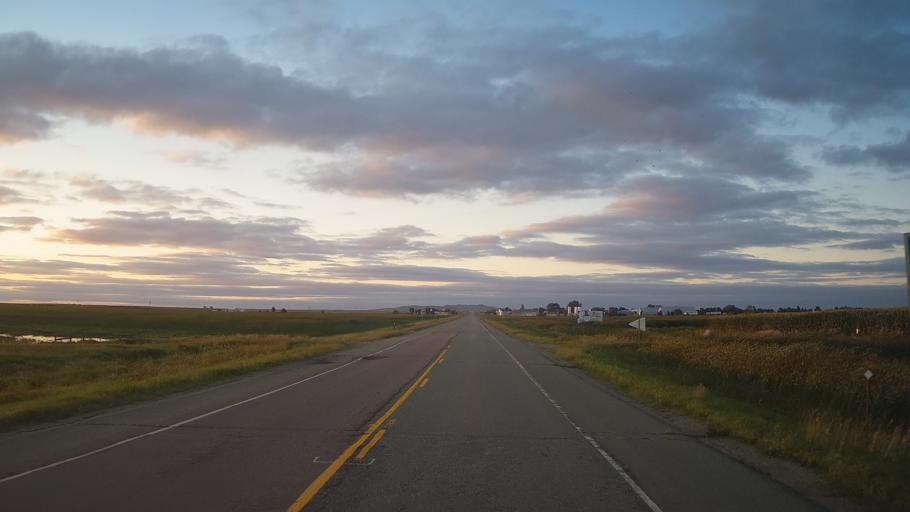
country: US
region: South Dakota
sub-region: Lyman County
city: Kennebec
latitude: 43.8670
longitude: -99.6061
